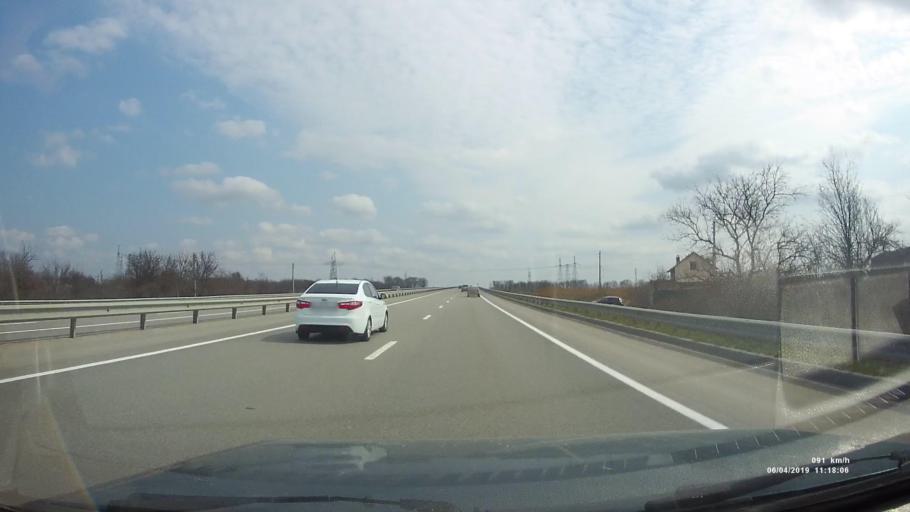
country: RU
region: Rostov
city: Kuleshovka
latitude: 47.0975
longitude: 39.5980
